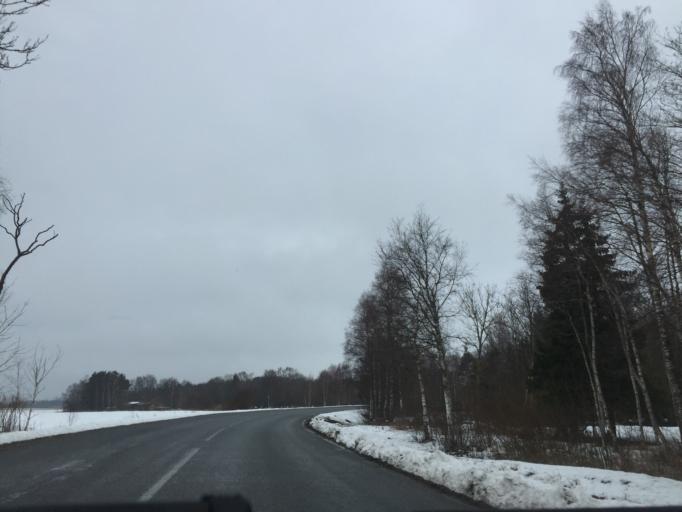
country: EE
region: Saare
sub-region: Kuressaare linn
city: Kuressaare
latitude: 58.3532
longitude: 22.0332
